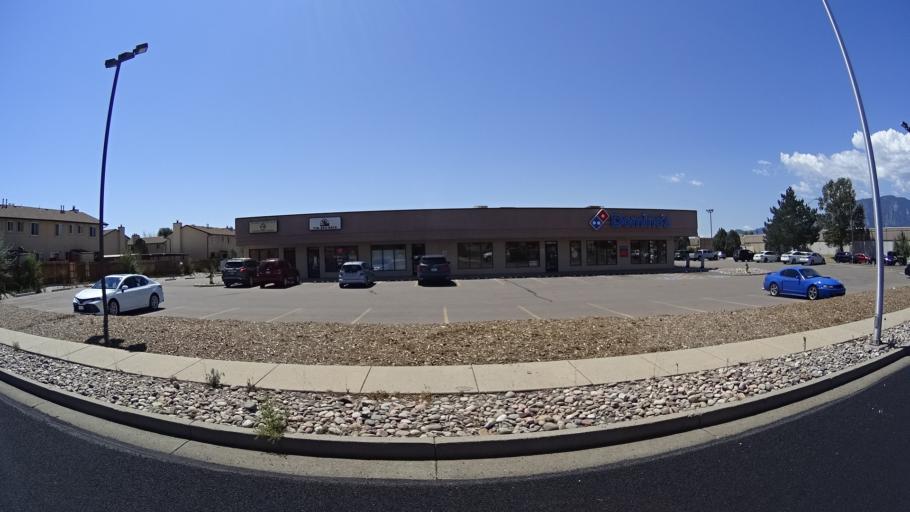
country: US
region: Colorado
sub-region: El Paso County
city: Stratmoor
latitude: 38.7890
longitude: -104.7535
